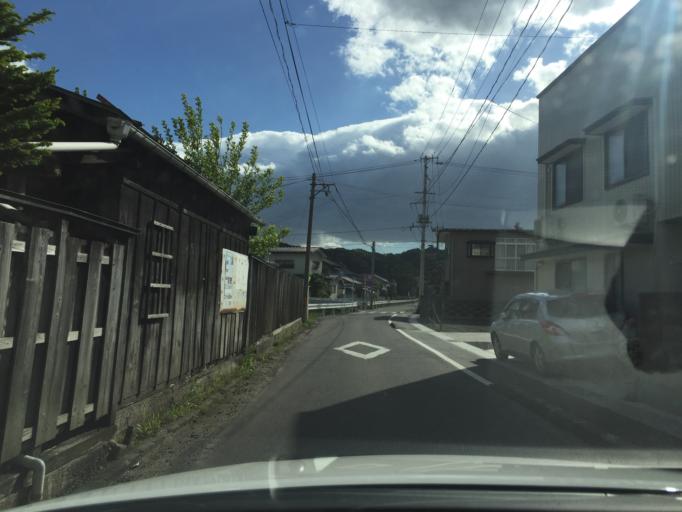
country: JP
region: Fukushima
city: Fukushima-shi
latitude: 37.6679
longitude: 140.6007
